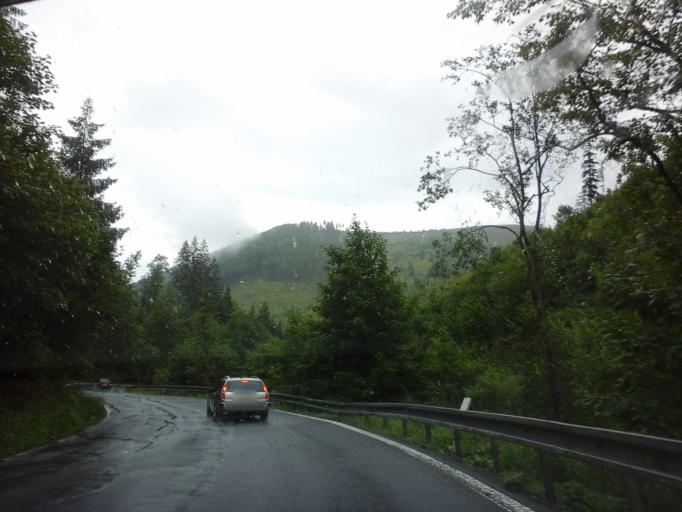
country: SK
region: Presovsky
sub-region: Okres Poprad
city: Poprad
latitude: 48.9504
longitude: 20.2942
